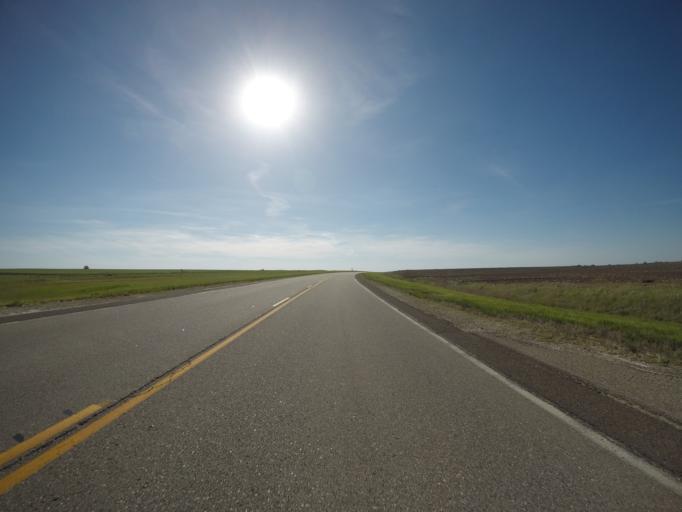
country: US
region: Kansas
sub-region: Clay County
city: Clay Center
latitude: 39.3645
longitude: -96.9424
